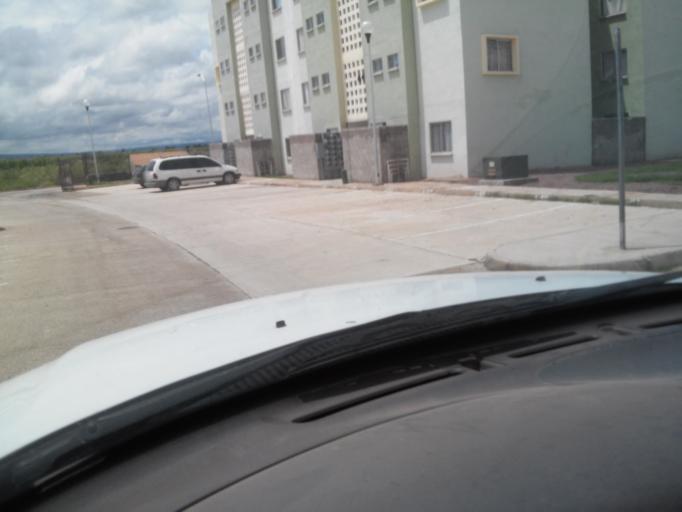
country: MX
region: Durango
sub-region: Durango
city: Jose Refugio Salcido
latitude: 24.0155
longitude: -104.5454
